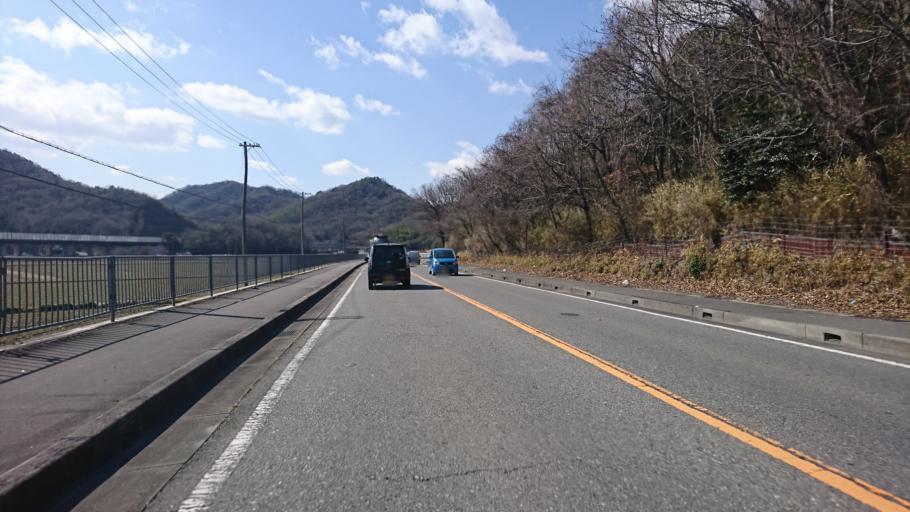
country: JP
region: Hyogo
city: Himeji
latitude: 34.8575
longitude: 134.7820
